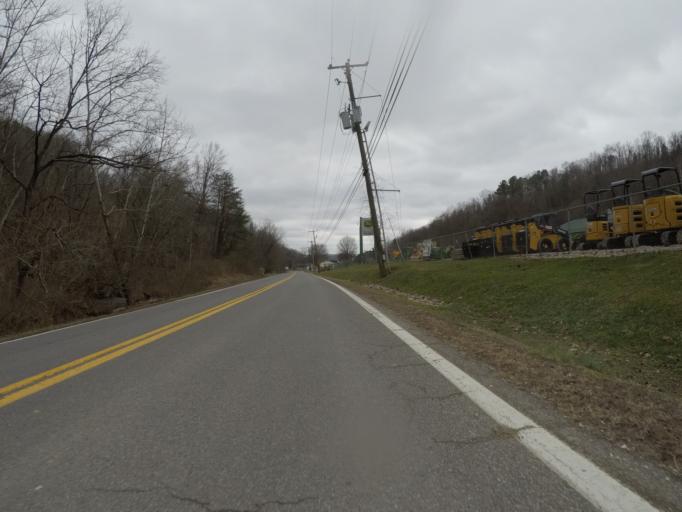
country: US
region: West Virginia
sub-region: Cabell County
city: Barboursville
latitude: 38.4322
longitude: -82.2940
